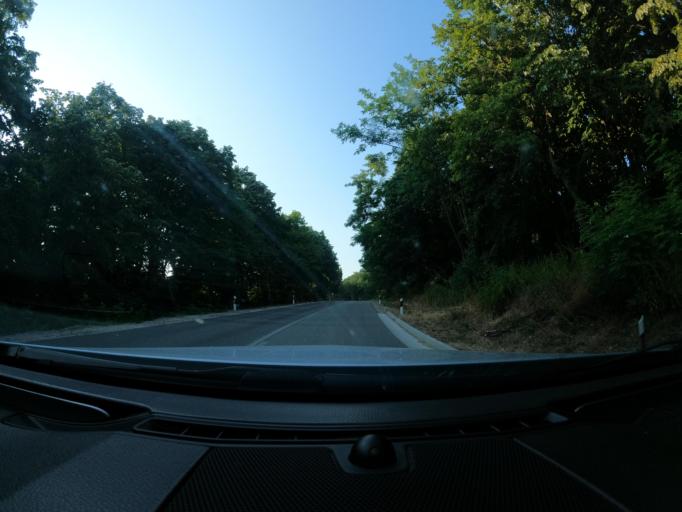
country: RS
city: Vrdnik
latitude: 45.1309
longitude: 19.7246
